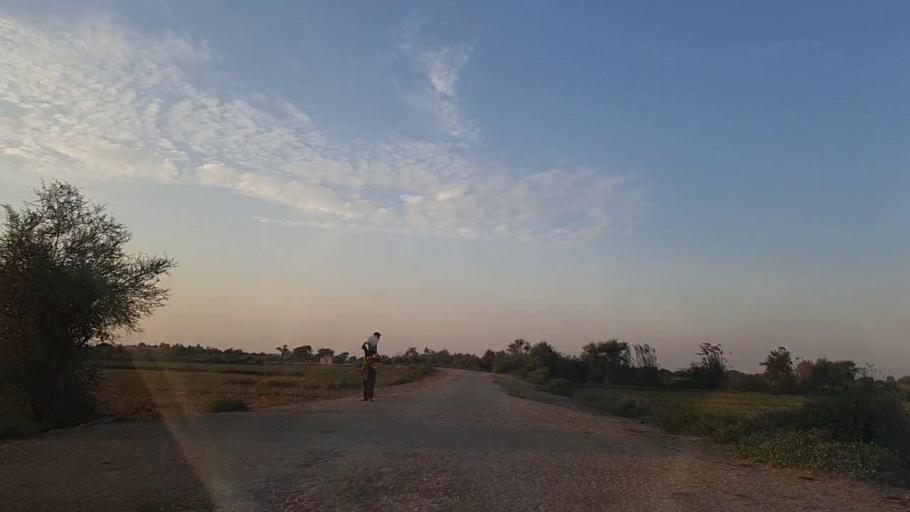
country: PK
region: Sindh
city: Chuhar Jamali
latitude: 24.4595
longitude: 68.1144
